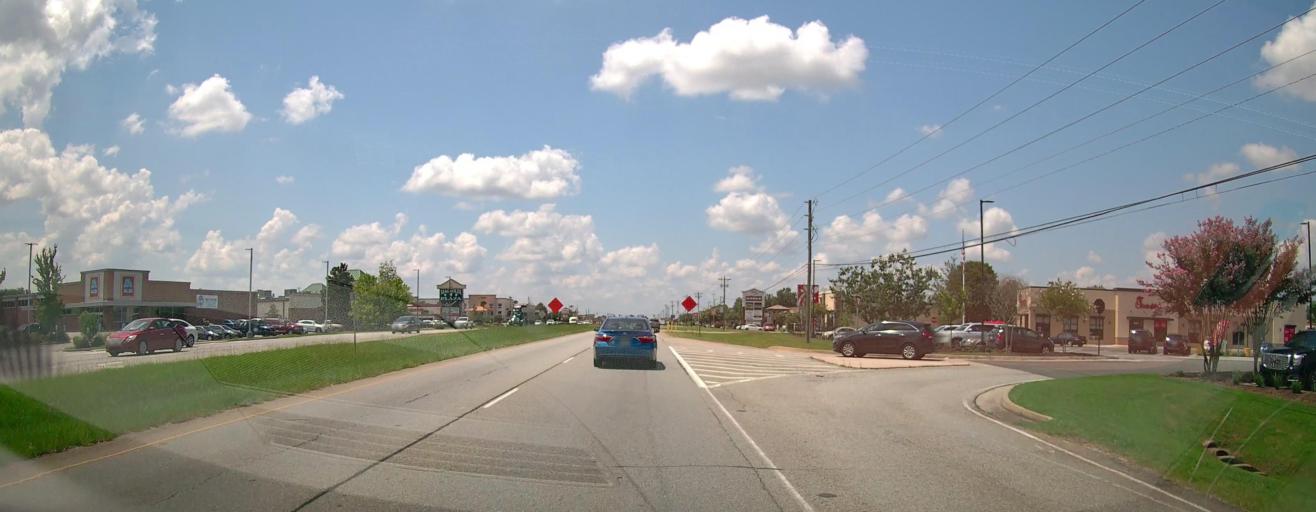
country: US
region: Georgia
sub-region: Houston County
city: Centerville
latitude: 32.6155
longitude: -83.6912
